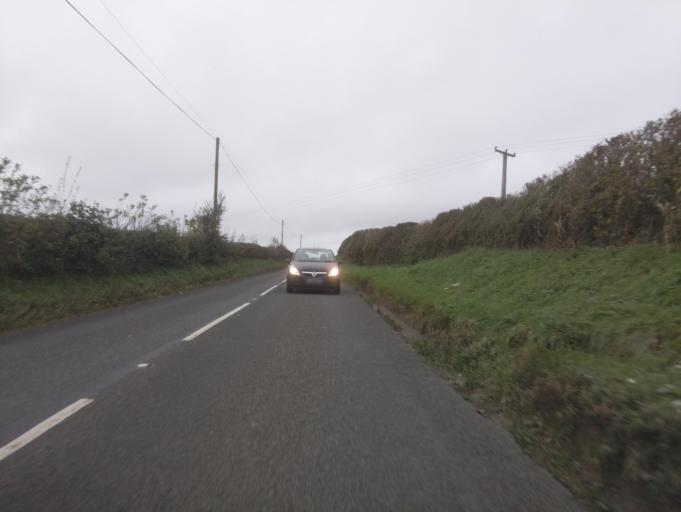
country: GB
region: England
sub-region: Dorset
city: Sherborne
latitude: 50.9575
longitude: -2.5392
